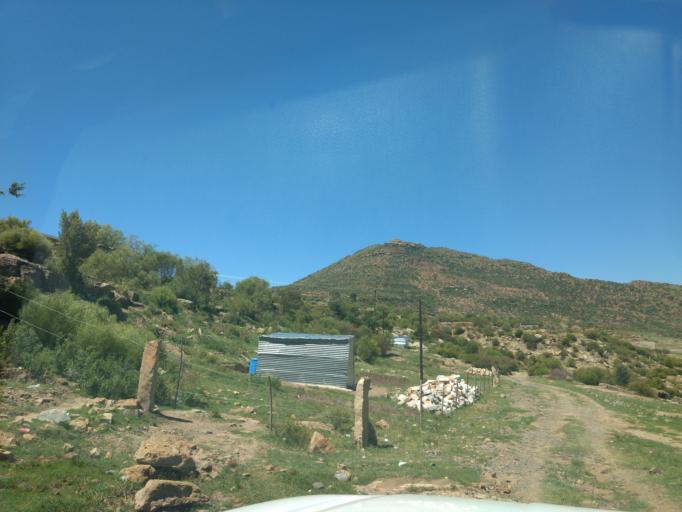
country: LS
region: Maseru
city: Maseru
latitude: -29.4584
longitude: 27.3719
